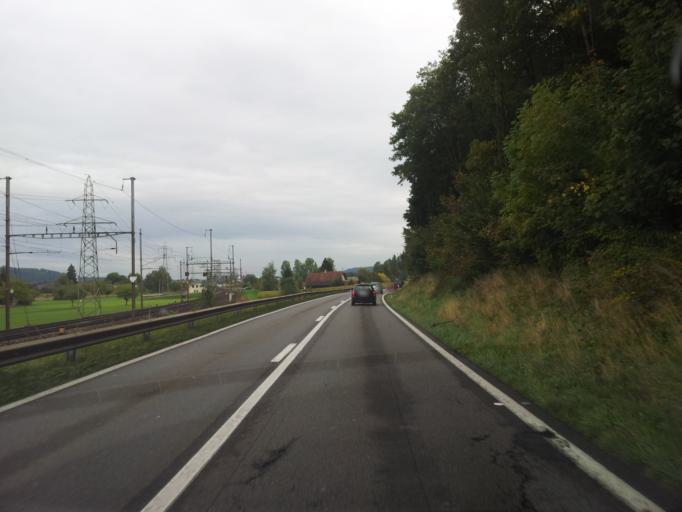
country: CH
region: Aargau
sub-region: Bezirk Lenzburg
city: Othmarsingen
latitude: 47.3862
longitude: 8.2113
